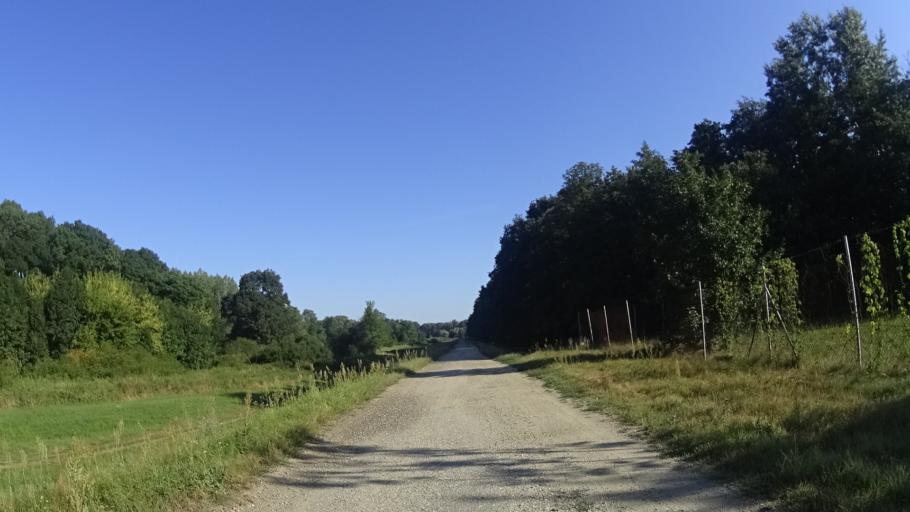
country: AT
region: Lower Austria
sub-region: Politischer Bezirk Mistelbach
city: Rabensburg
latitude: 48.6473
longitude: 16.9774
